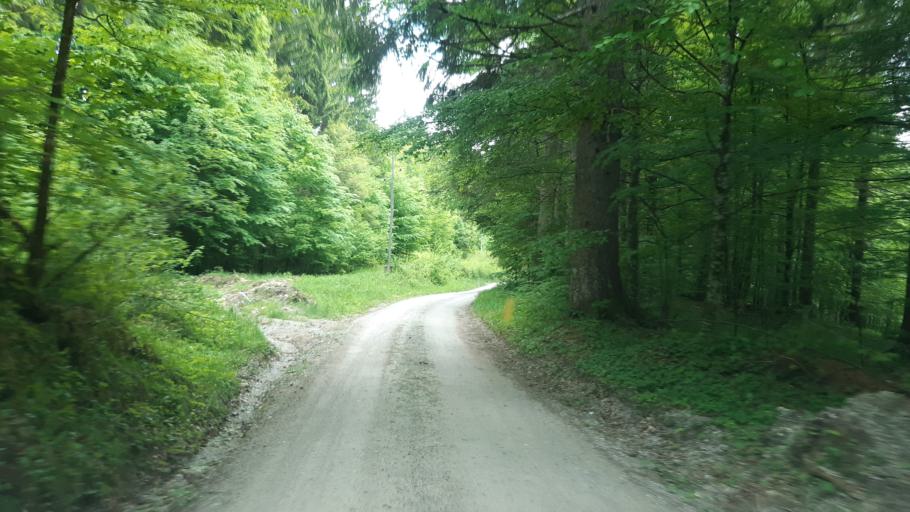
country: SI
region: Dolenjske Toplice
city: Dolenjske Toplice
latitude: 45.6154
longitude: 15.0157
